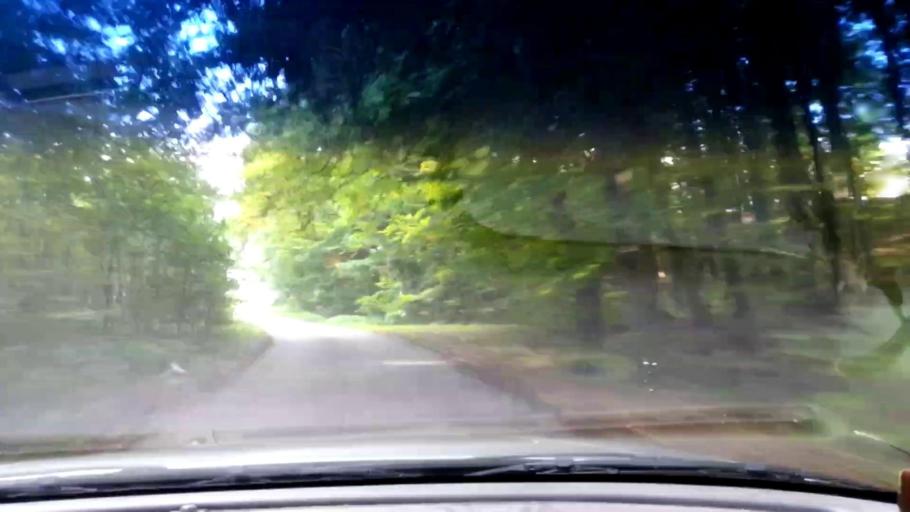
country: DE
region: Bavaria
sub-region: Upper Franconia
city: Schesslitz
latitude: 49.9887
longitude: 11.0838
